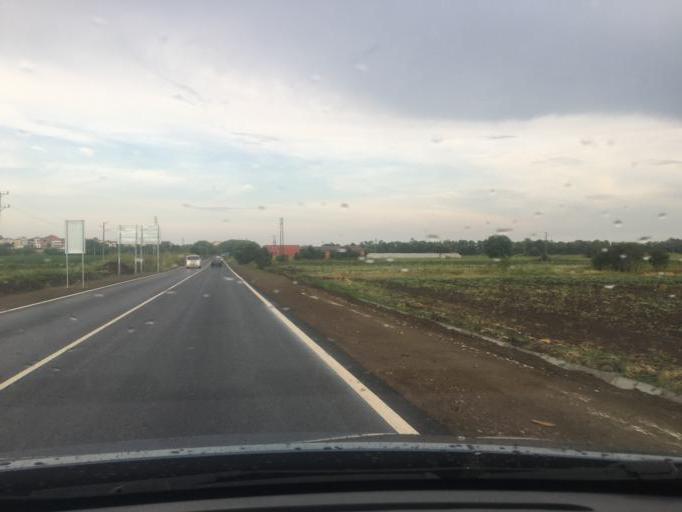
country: BG
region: Burgas
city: Aheloy
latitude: 42.6455
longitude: 27.6377
